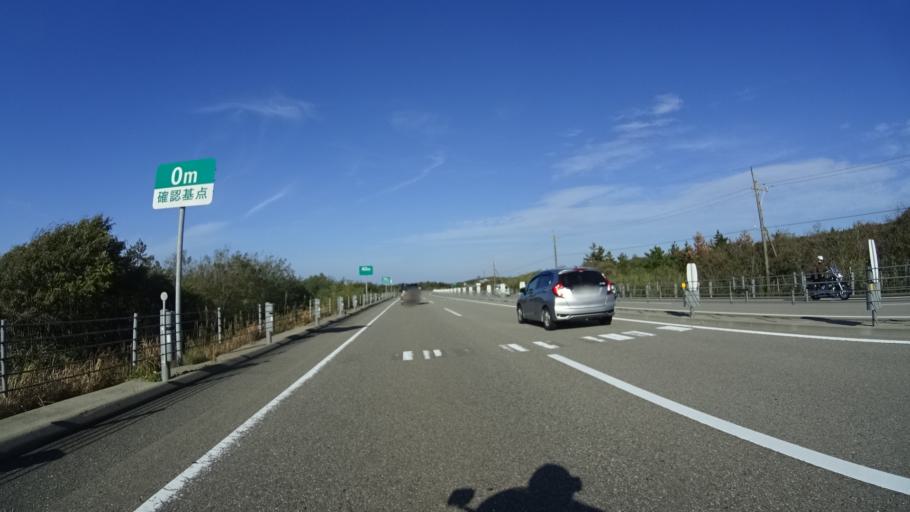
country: JP
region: Ishikawa
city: Tsubata
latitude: 36.7039
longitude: 136.6749
